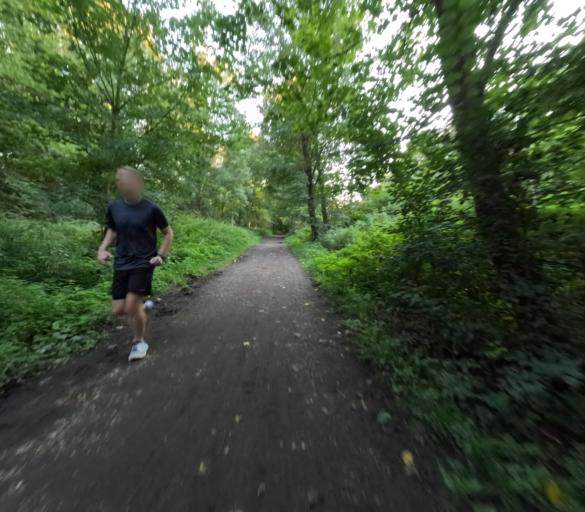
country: DE
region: Saxony
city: Leipzig
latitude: 51.3615
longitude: 12.3232
